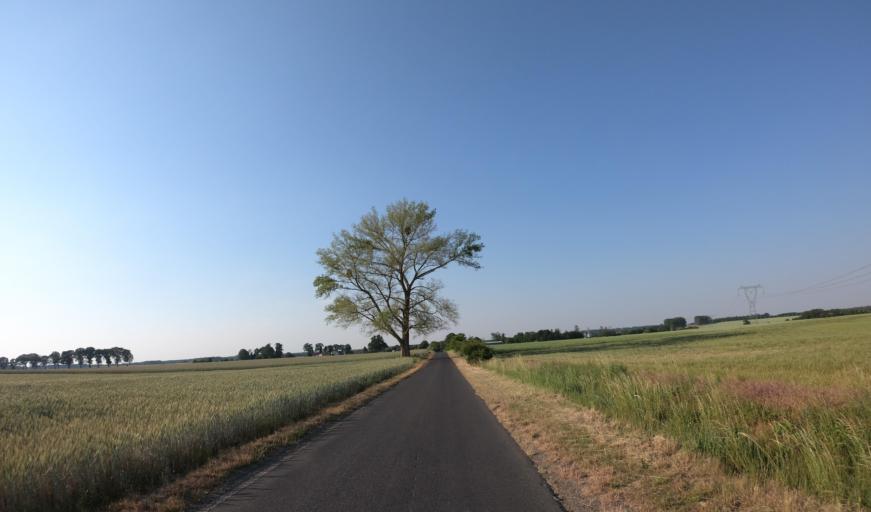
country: PL
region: West Pomeranian Voivodeship
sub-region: Powiat lobeski
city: Radowo Male
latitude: 53.6513
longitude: 15.4105
